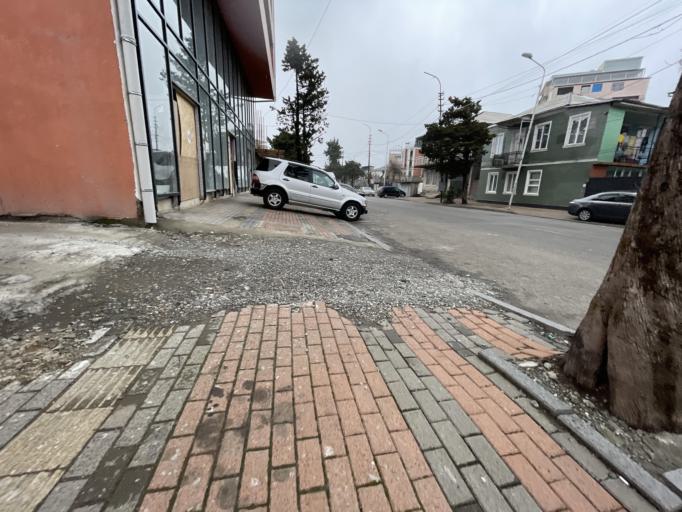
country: GE
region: Ajaria
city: Batumi
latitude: 41.6366
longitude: 41.6445
